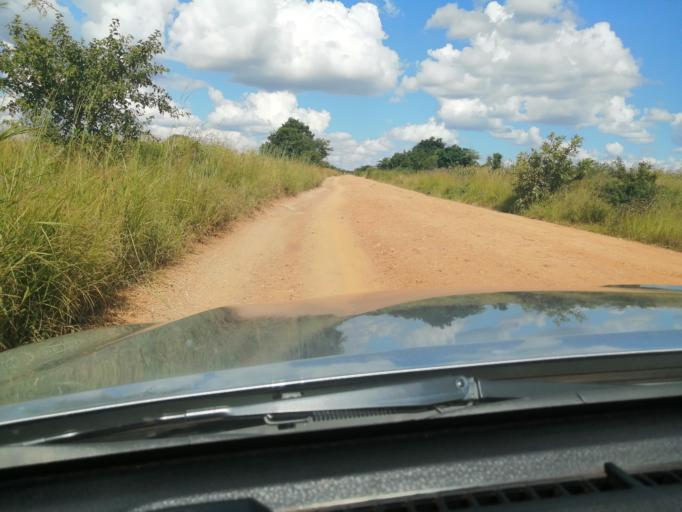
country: ZM
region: Lusaka
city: Lusaka
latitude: -15.2056
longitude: 28.0779
